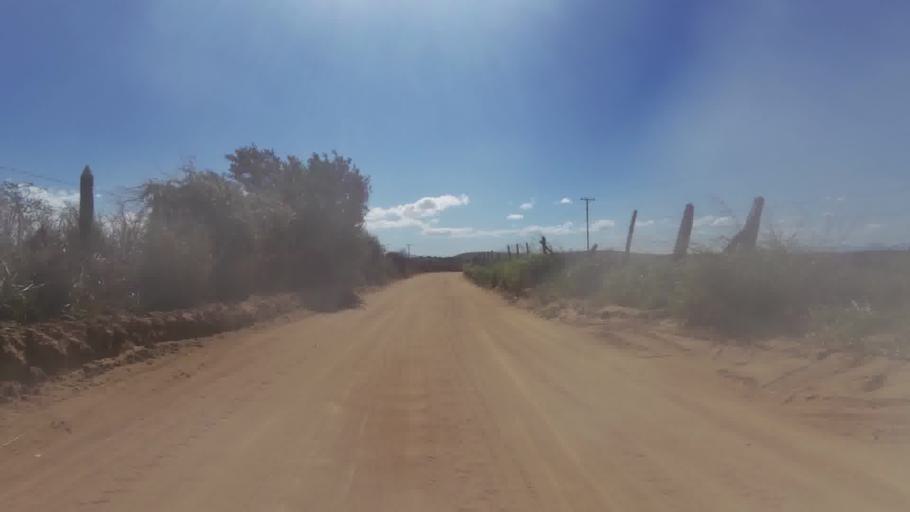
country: BR
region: Espirito Santo
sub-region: Marataizes
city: Marataizes
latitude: -21.1556
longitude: -40.9818
